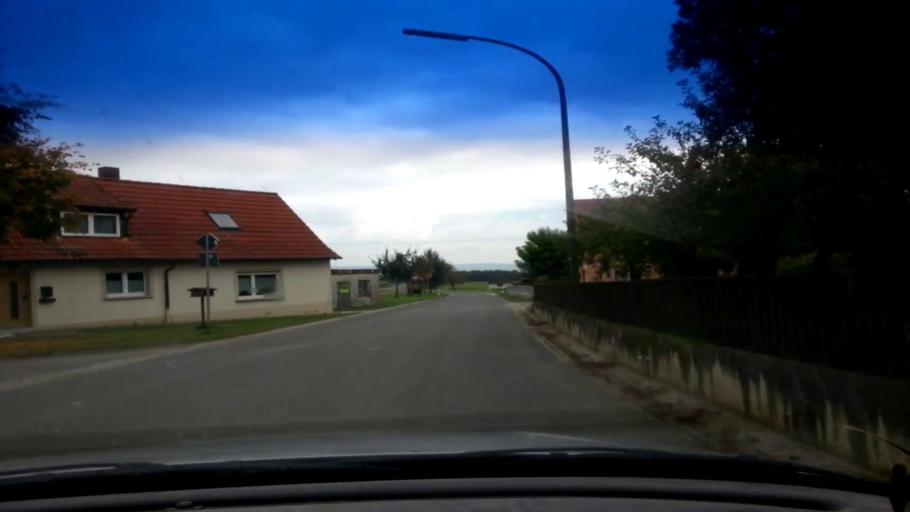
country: DE
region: Bavaria
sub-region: Upper Franconia
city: Zapfendorf
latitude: 49.9883
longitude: 10.9516
